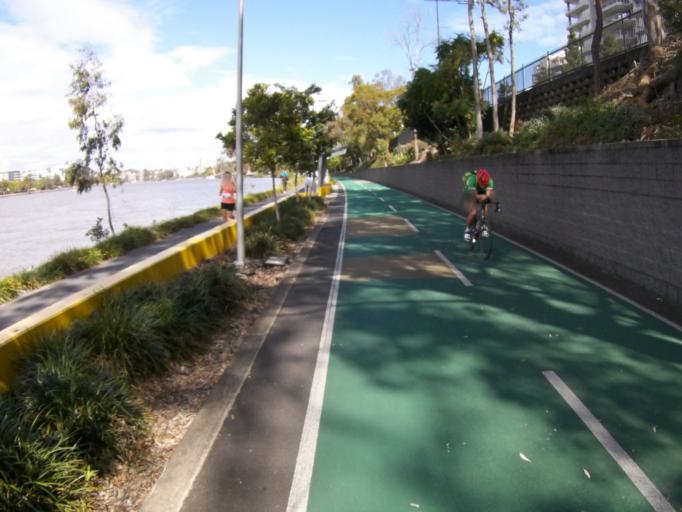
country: AU
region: Queensland
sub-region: Brisbane
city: Milton
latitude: -27.4772
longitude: 153.0013
